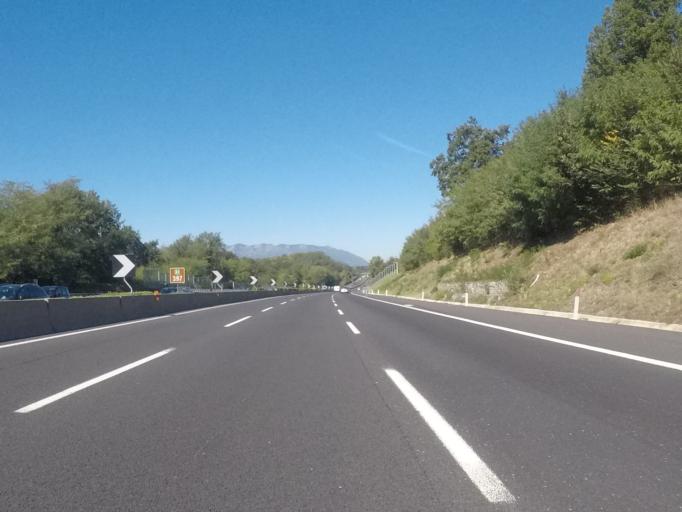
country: IT
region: Latium
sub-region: Provincia di Frosinone
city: Pofi
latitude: 41.5586
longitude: 13.4117
